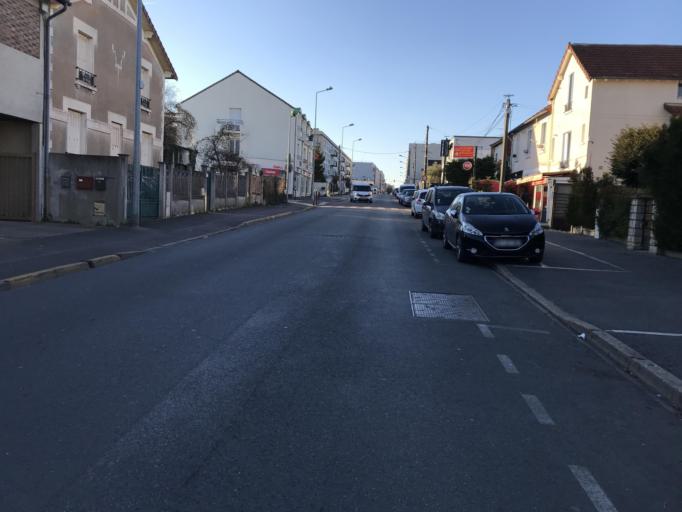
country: FR
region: Ile-de-France
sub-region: Departement de l'Essonne
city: Morangis
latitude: 48.7010
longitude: 2.3238
